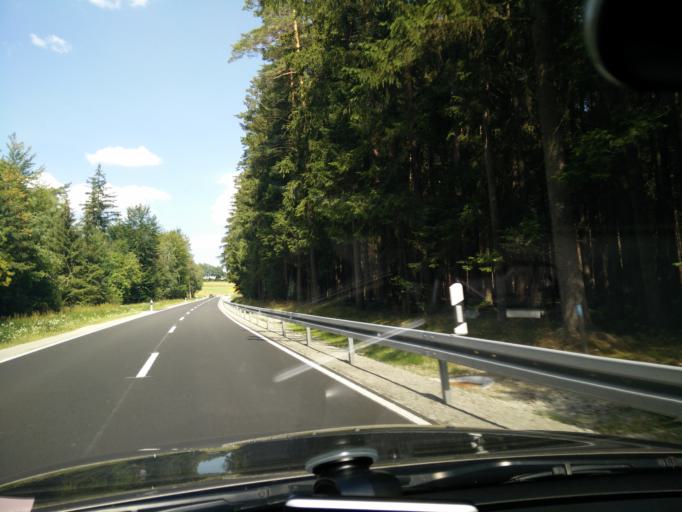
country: DE
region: Bavaria
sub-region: Upper Franconia
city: Wunsiedel
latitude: 50.0469
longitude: 11.9749
